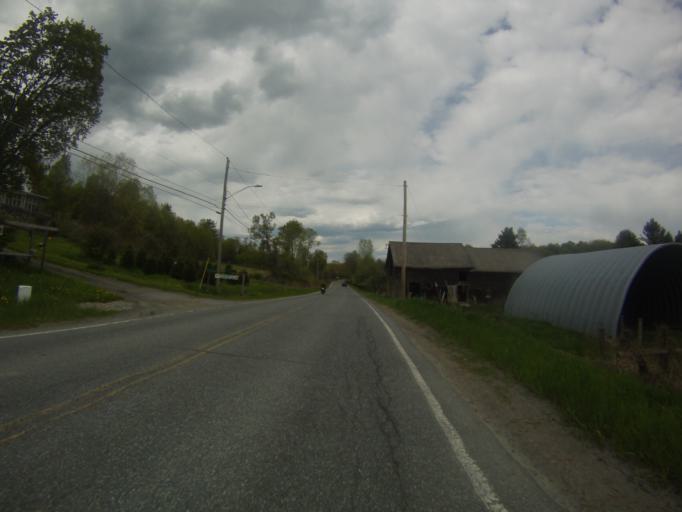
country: US
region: New York
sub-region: Essex County
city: Port Henry
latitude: 44.0323
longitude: -73.5024
